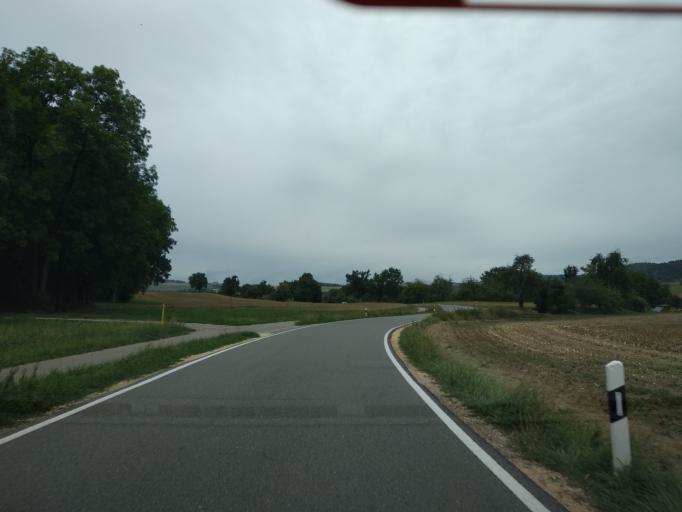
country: DE
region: Baden-Wuerttemberg
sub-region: Freiburg Region
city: Hilzingen
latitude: 47.7505
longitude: 8.7890
